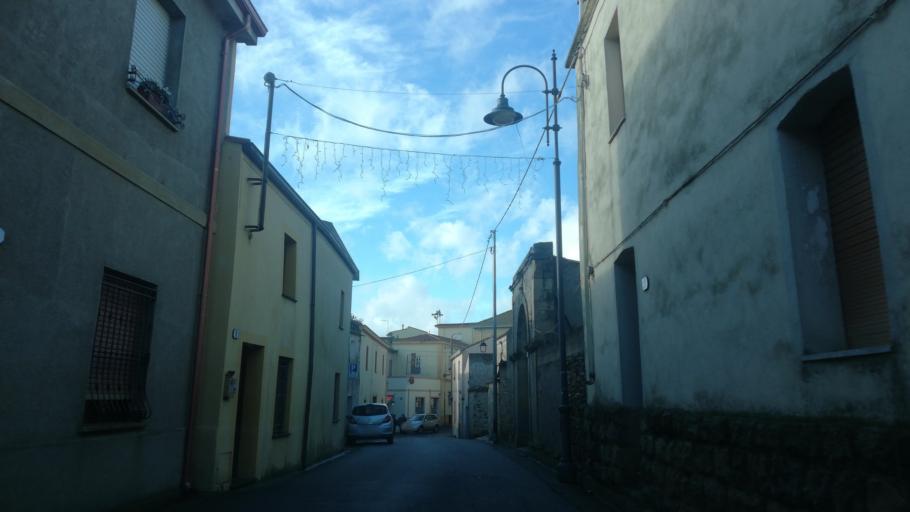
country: IT
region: Sardinia
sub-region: Provincia di Medio Campidano
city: Villanovaforru
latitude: 39.6324
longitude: 8.8697
